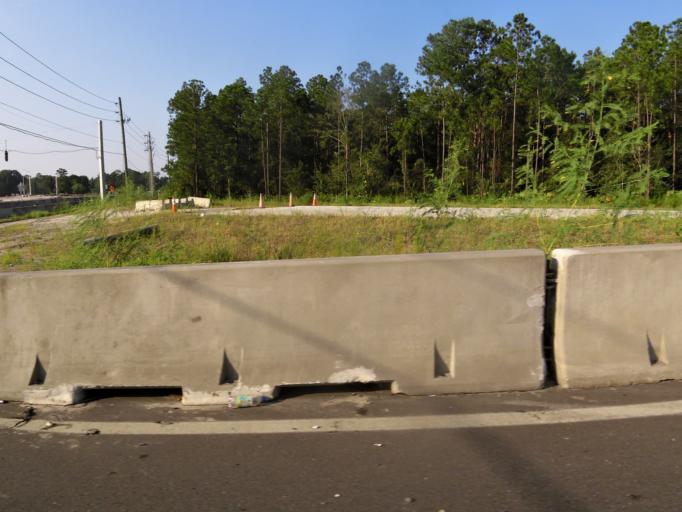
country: US
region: Florida
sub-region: Duval County
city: Baldwin
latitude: 30.2904
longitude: -81.9826
